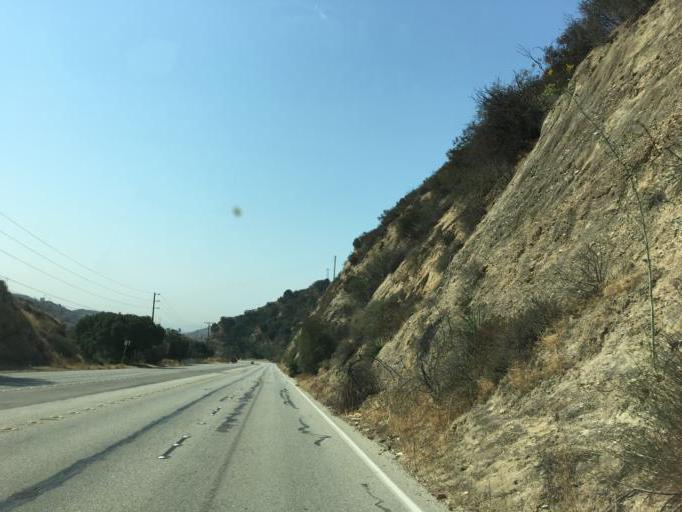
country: US
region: California
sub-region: Los Angeles County
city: Santa Clarita
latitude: 34.3436
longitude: -118.5100
